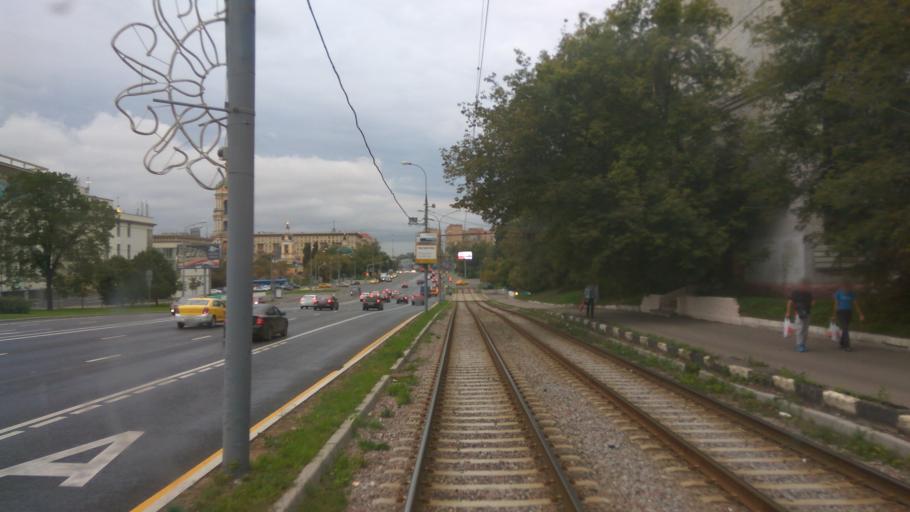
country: RU
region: Moscow
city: Taganskiy
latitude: 55.7287
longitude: 37.6623
